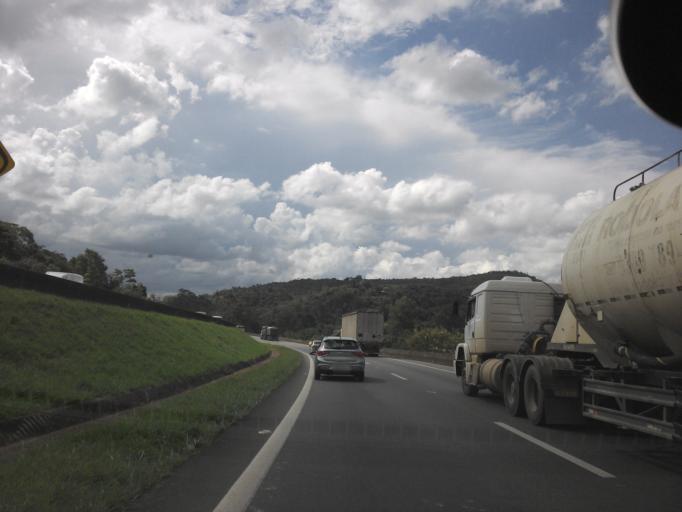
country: BR
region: Sao Paulo
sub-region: Valinhos
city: Valinhos
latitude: -22.9229
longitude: -46.9423
